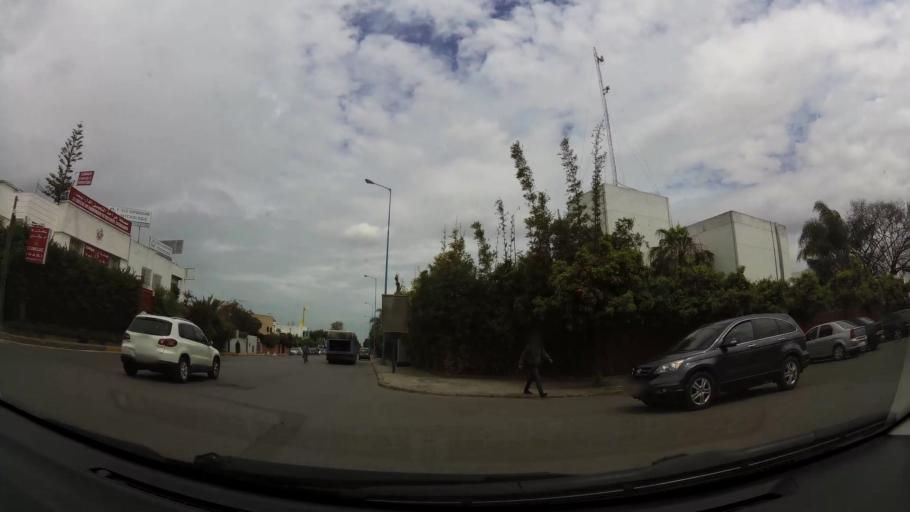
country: MA
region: Grand Casablanca
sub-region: Casablanca
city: Casablanca
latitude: 33.5738
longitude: -7.6647
